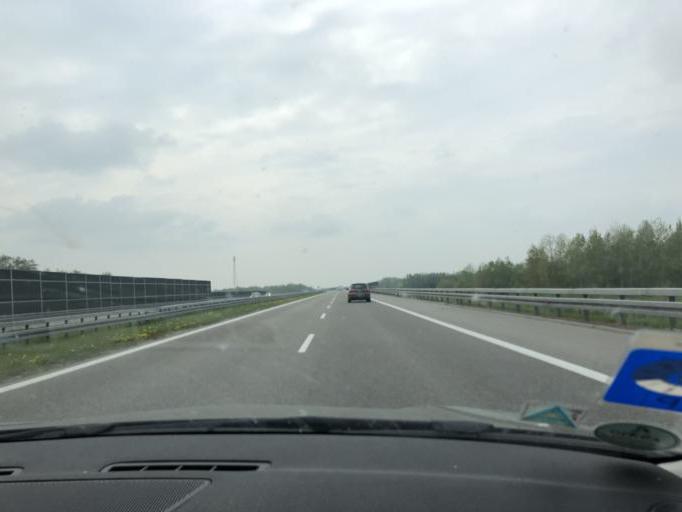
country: PL
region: Subcarpathian Voivodeship
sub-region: Powiat ropczycko-sedziszowski
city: Ostrow
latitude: 50.1086
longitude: 21.6347
